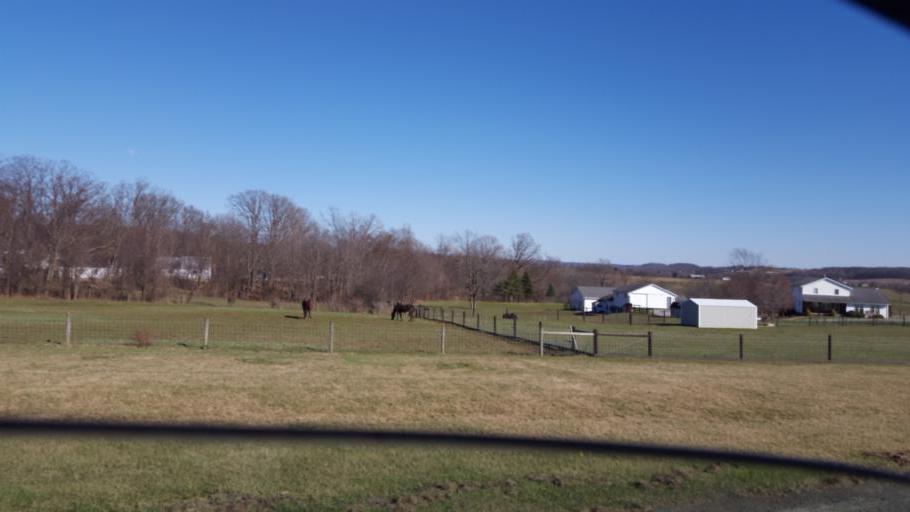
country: US
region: Ohio
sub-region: Wayne County
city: Dalton
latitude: 40.7278
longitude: -81.6956
